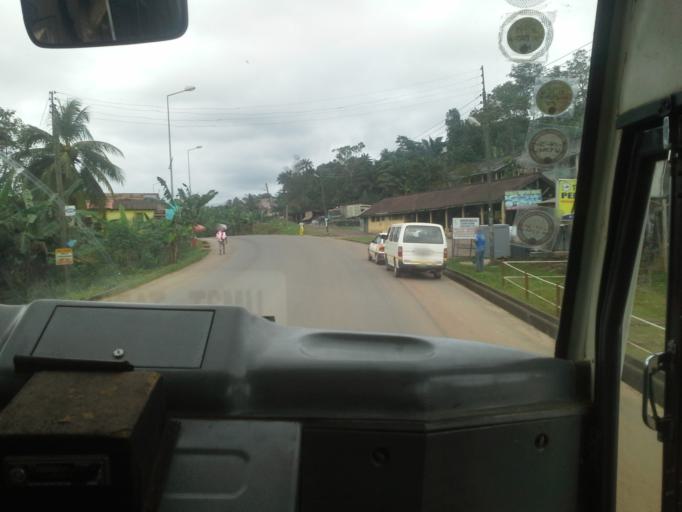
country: GH
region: Western
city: Tarkwa
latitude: 5.3092
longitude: -1.9934
